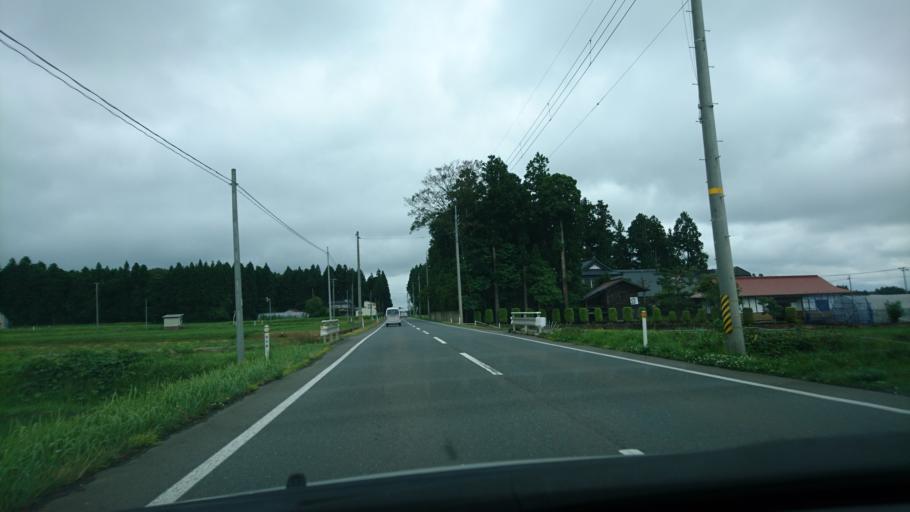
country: JP
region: Iwate
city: Mizusawa
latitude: 39.1153
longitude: 141.0529
